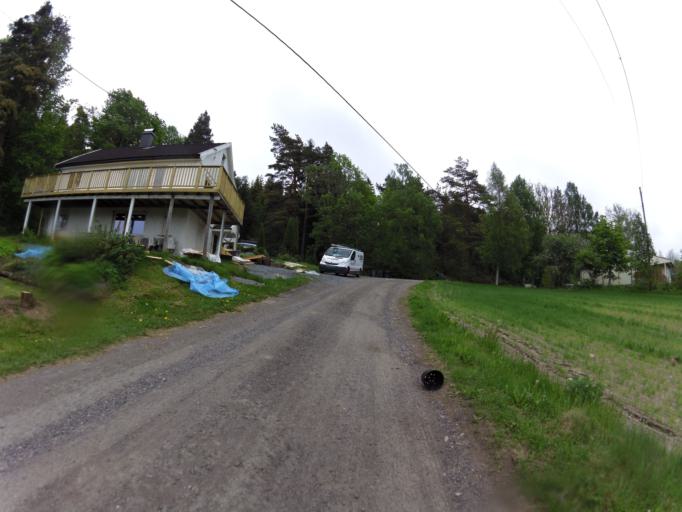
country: NO
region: Ostfold
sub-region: Rygge
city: Larkollen
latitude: 59.3634
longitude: 10.6946
